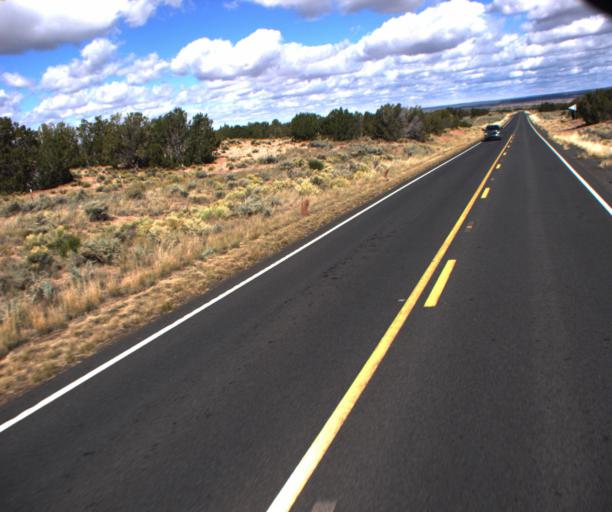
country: US
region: Arizona
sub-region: Apache County
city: Houck
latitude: 35.1460
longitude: -109.3335
